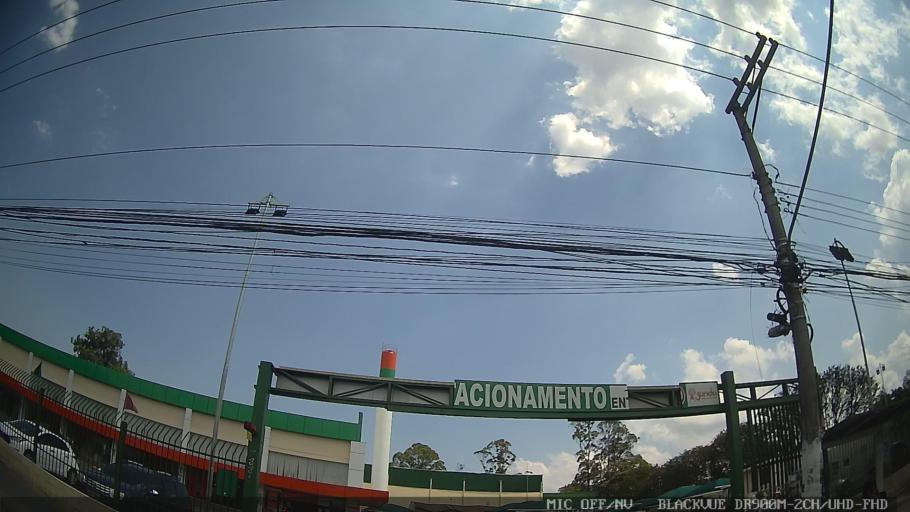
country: BR
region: Sao Paulo
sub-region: Taboao Da Serra
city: Taboao da Serra
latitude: -23.6763
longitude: -46.7901
